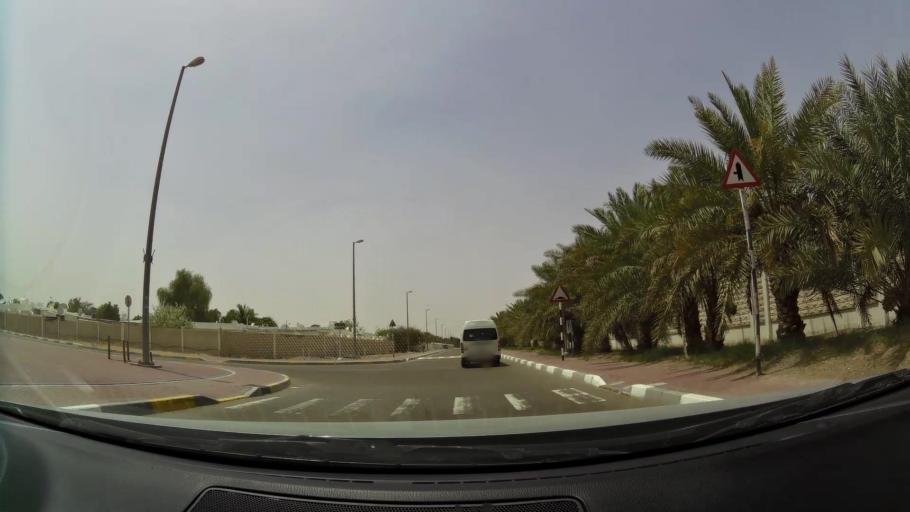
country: AE
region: Abu Dhabi
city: Al Ain
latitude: 24.1851
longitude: 55.6760
